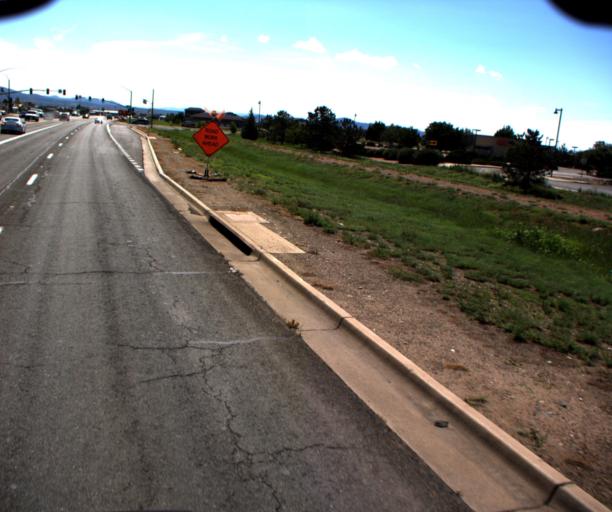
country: US
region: Arizona
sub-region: Yavapai County
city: Prescott Valley
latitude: 34.5858
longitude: -112.3198
